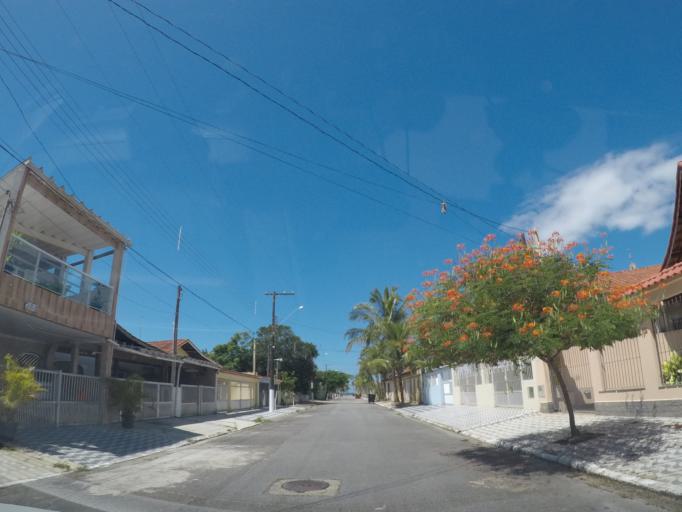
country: BR
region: Sao Paulo
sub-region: Mongagua
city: Mongagua
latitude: -24.0740
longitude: -46.5804
